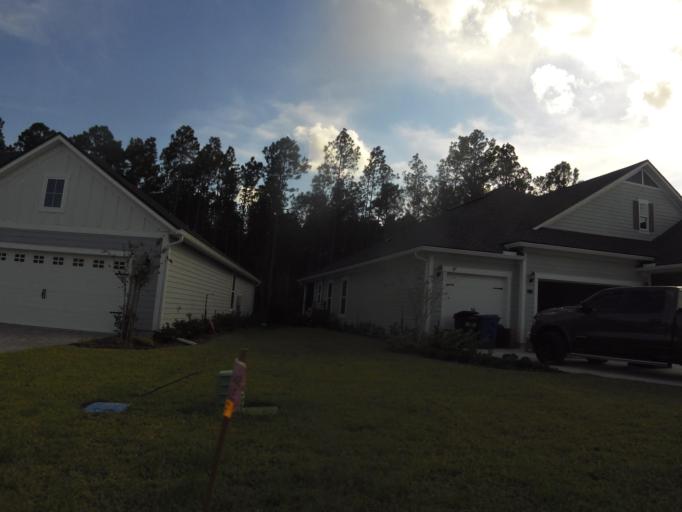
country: US
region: Florida
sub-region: Clay County
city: Green Cove Springs
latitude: 29.9274
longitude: -81.5132
